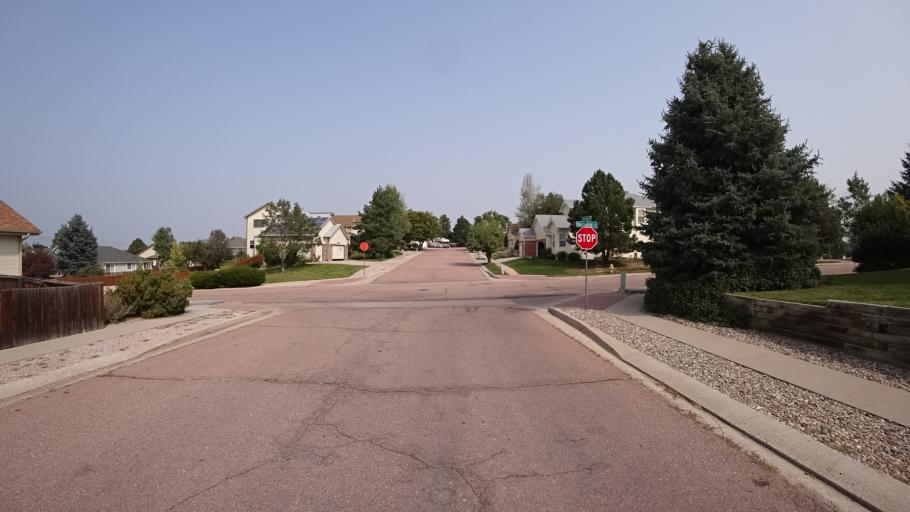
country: US
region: Colorado
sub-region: El Paso County
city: Cimarron Hills
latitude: 38.9151
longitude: -104.7399
